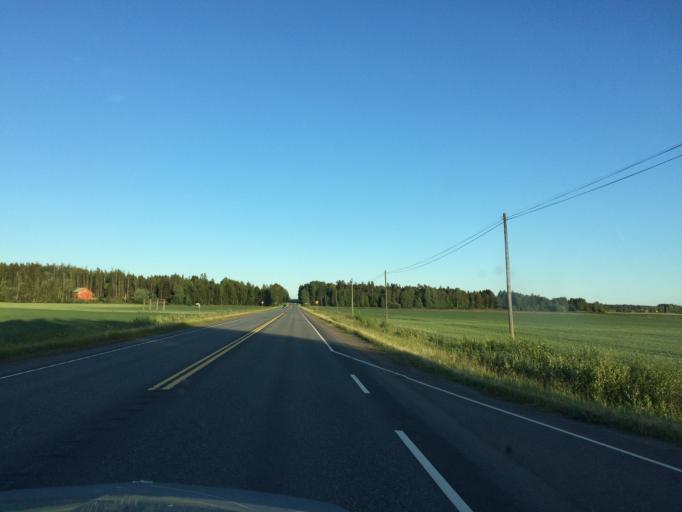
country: FI
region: Haeme
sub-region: Haemeenlinna
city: Tervakoski
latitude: 60.7977
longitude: 24.6654
